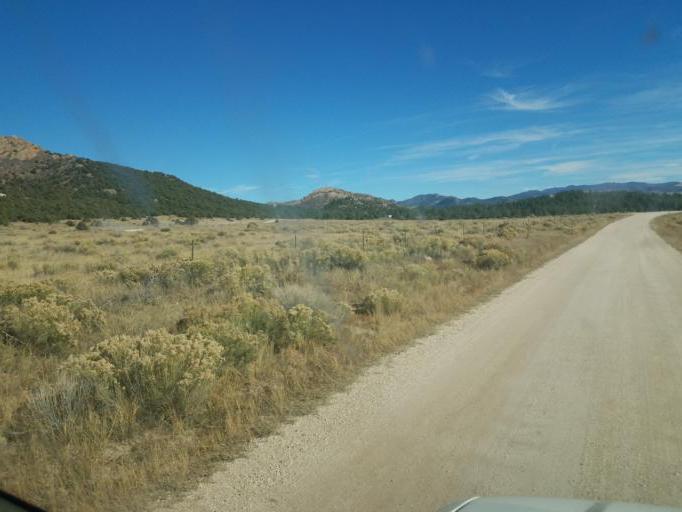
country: US
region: Colorado
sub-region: Custer County
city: Westcliffe
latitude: 38.2339
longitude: -105.4590
